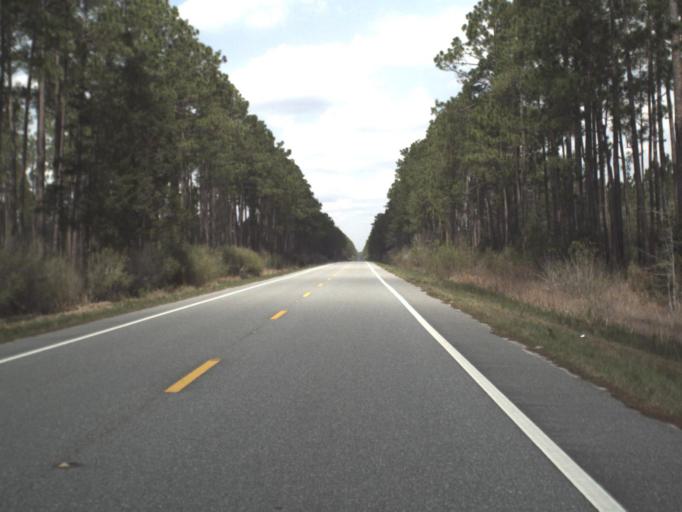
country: US
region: Florida
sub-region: Franklin County
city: Apalachicola
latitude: 29.8607
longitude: -84.9739
